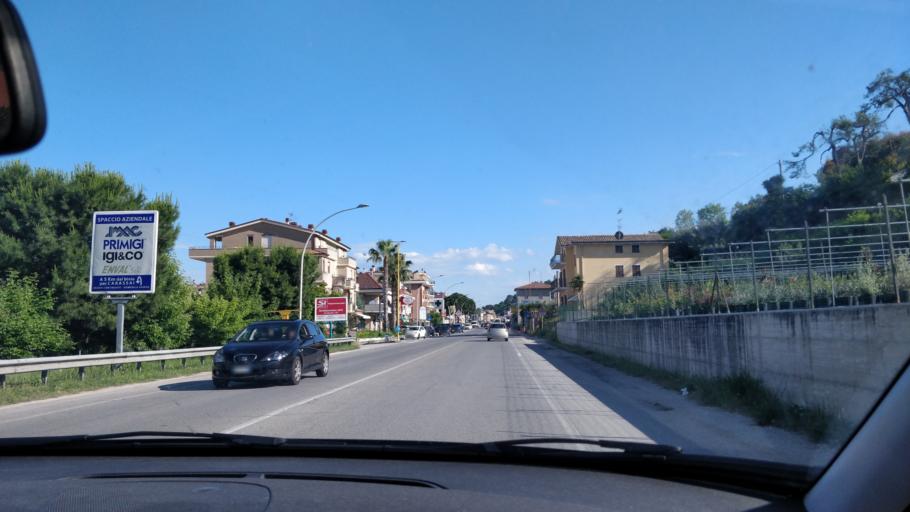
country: IT
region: The Marches
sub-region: Provincia di Ascoli Piceno
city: Cupra Marittima
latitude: 43.0335
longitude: 13.8563
